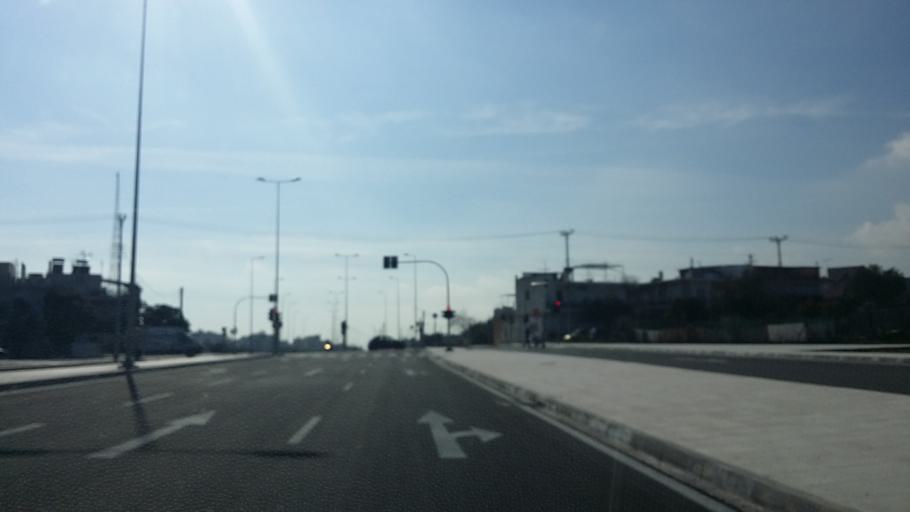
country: GR
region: Attica
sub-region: Nomarchia Athinas
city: Kamateron
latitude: 38.0437
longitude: 23.7110
